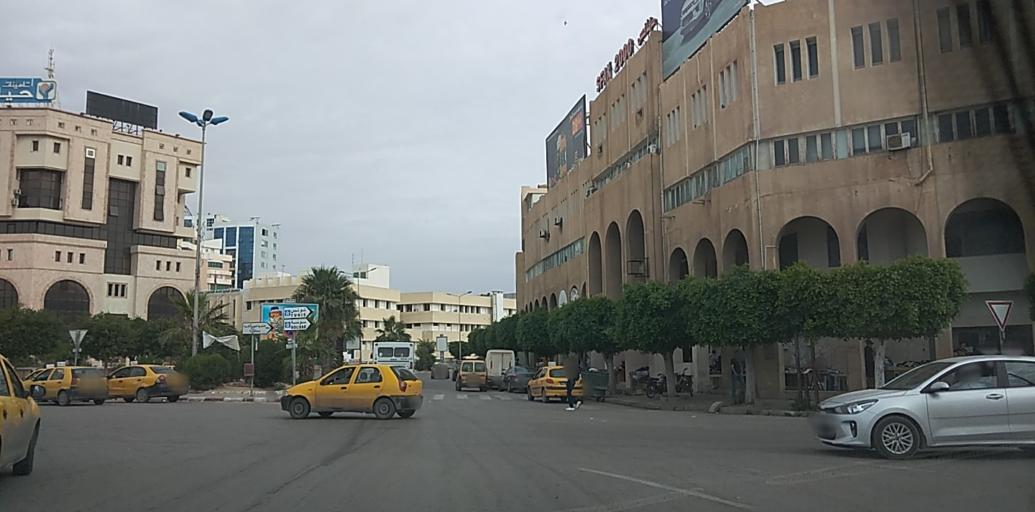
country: TN
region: Safaqis
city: Sfax
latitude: 34.7402
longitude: 10.7604
